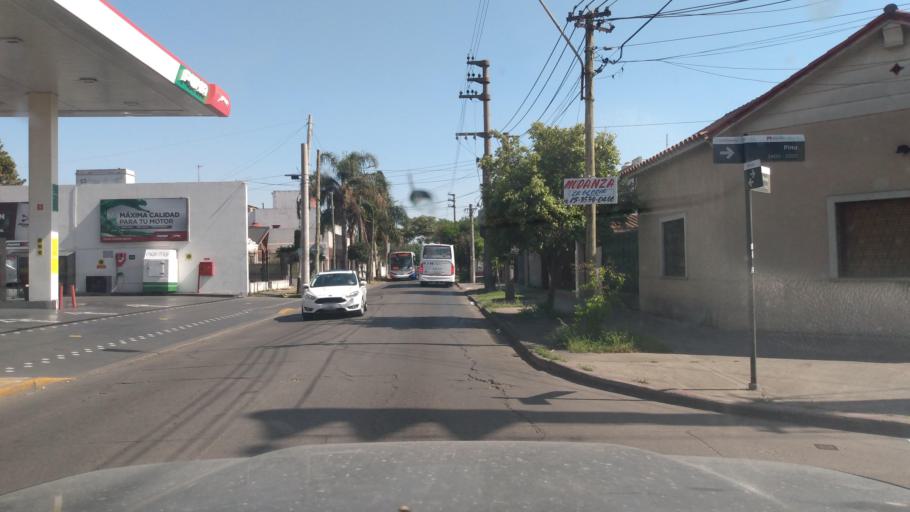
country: AR
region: Buenos Aires
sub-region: Partido de Moron
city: Moron
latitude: -34.6352
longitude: -58.5978
